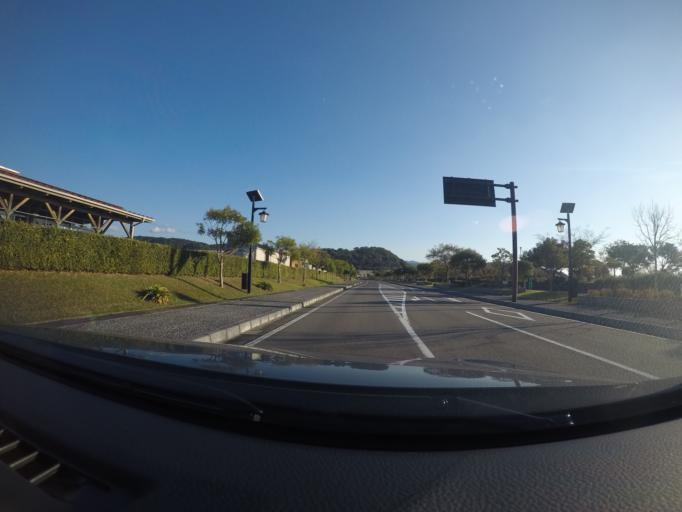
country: JP
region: Kumamoto
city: Minamata
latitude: 32.2022
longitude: 130.3814
